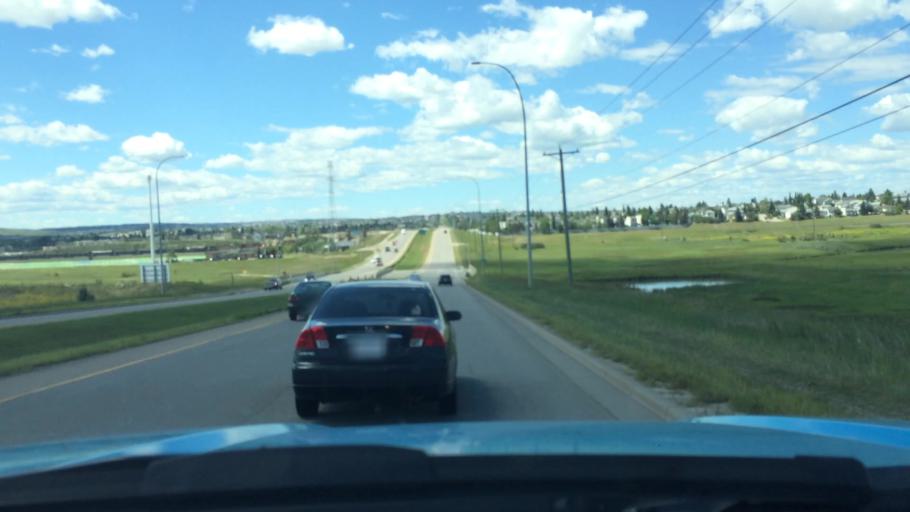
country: CA
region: Alberta
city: Calgary
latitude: 51.1544
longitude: -114.0312
